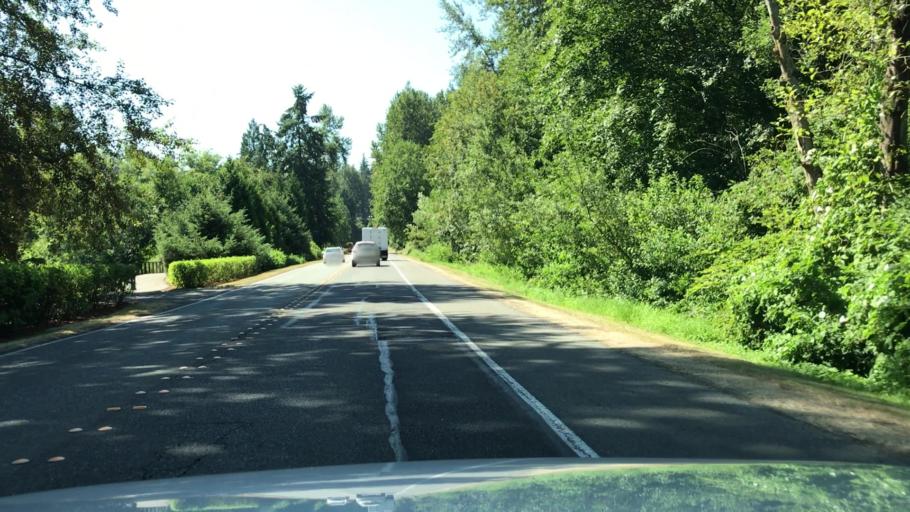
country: US
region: Washington
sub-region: King County
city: Eastgate
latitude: 47.5955
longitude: -122.1319
